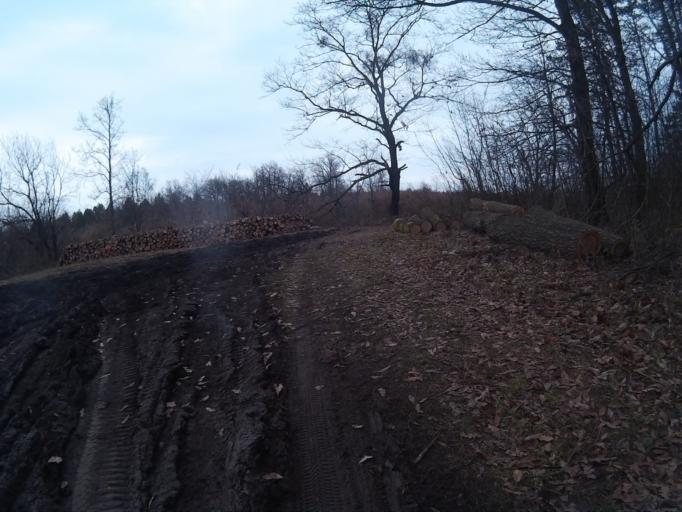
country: HU
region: Veszprem
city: Tapolca
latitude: 46.9827
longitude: 17.4914
